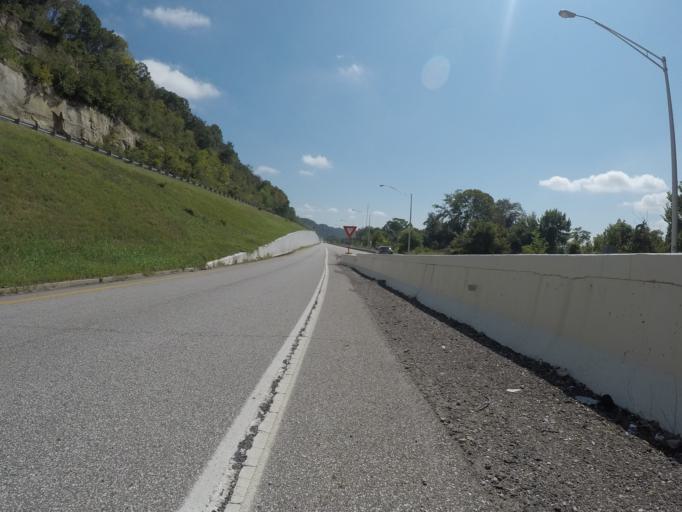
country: US
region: Kentucky
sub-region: Boyd County
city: Ashland
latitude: 38.4853
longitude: -82.6368
